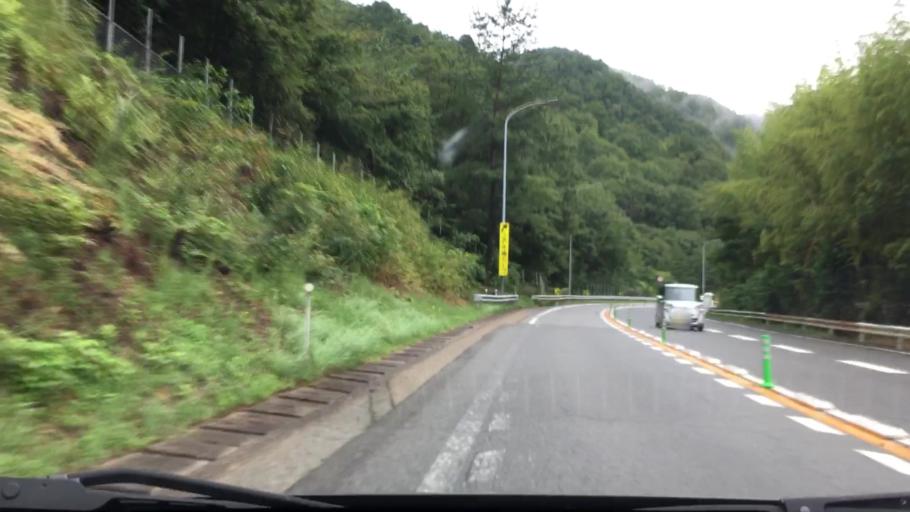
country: JP
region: Hyogo
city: Nishiwaki
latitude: 35.0191
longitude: 134.7663
